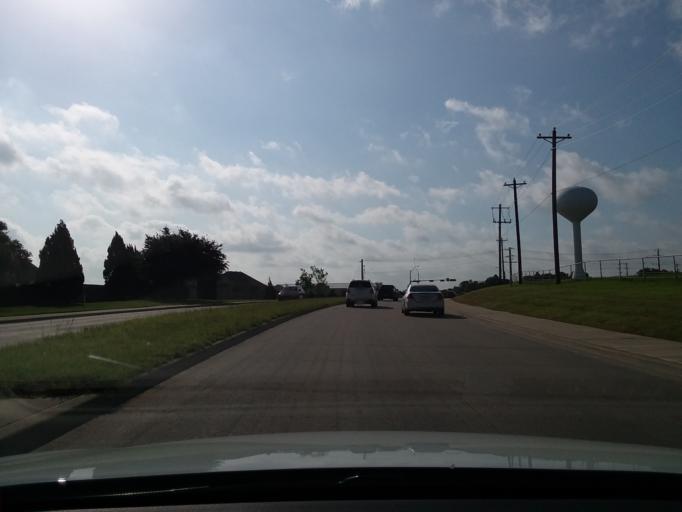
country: US
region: Texas
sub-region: Denton County
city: Double Oak
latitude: 33.0738
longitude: -97.1157
